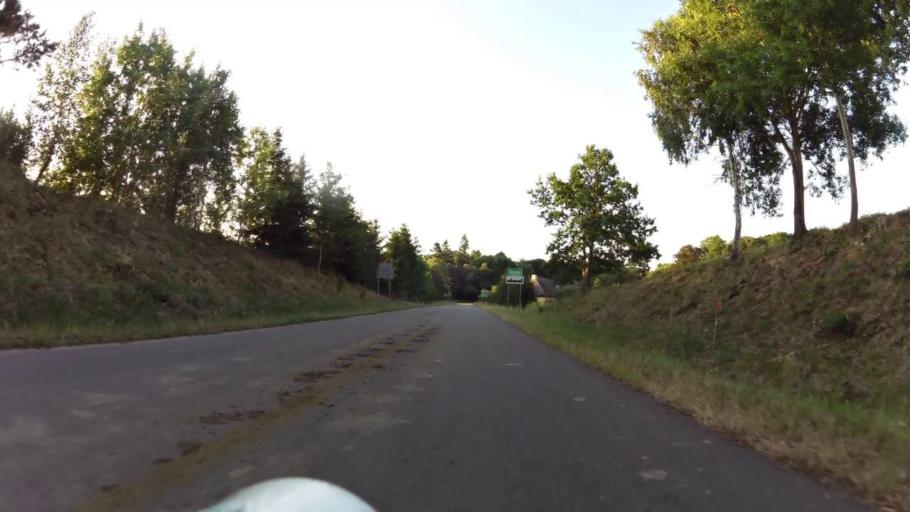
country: PL
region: West Pomeranian Voivodeship
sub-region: Powiat szczecinecki
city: Bialy Bor
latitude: 53.8593
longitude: 16.7169
